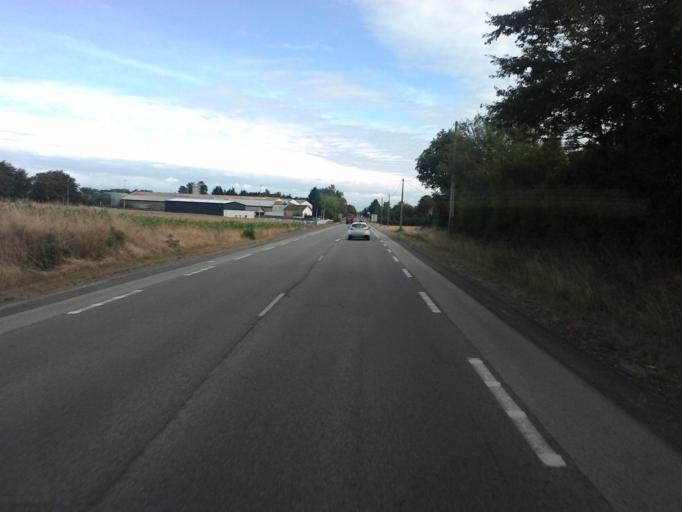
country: FR
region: Rhone-Alpes
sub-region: Departement de l'Ain
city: Tossiat
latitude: 46.1300
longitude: 5.2911
